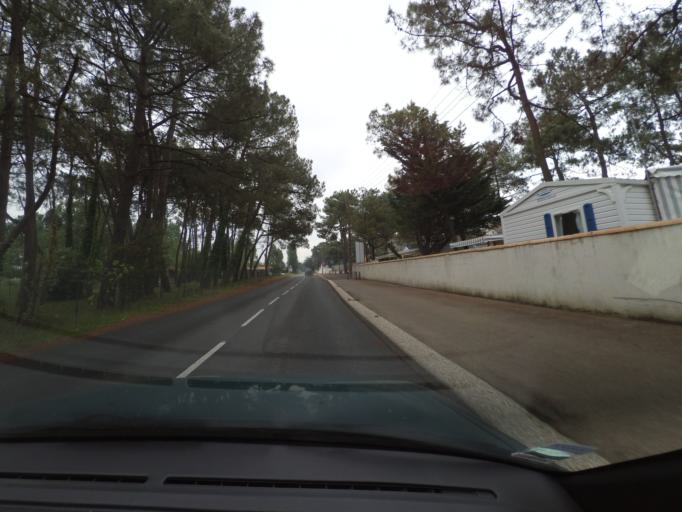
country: FR
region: Pays de la Loire
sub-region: Departement de la Vendee
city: Angles
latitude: 46.3462
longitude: -1.3511
